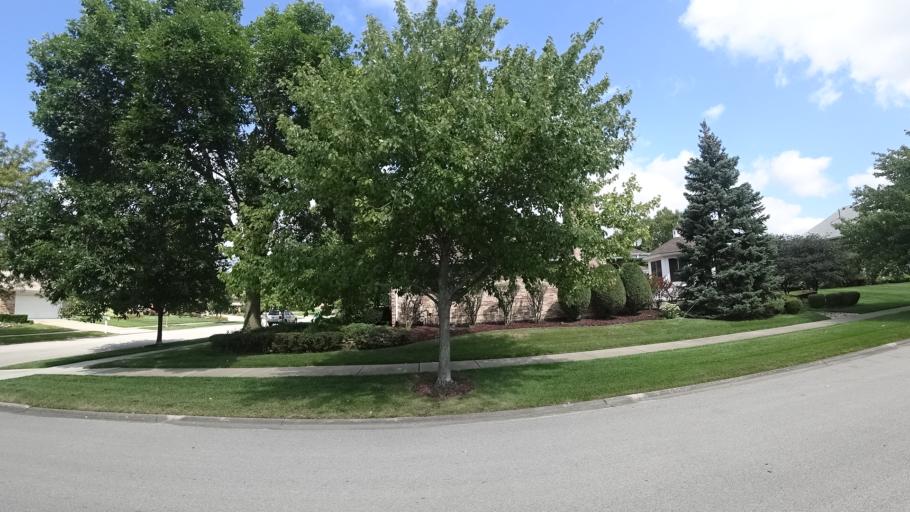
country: US
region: Illinois
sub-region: Will County
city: Mokena
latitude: 41.5607
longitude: -87.8761
